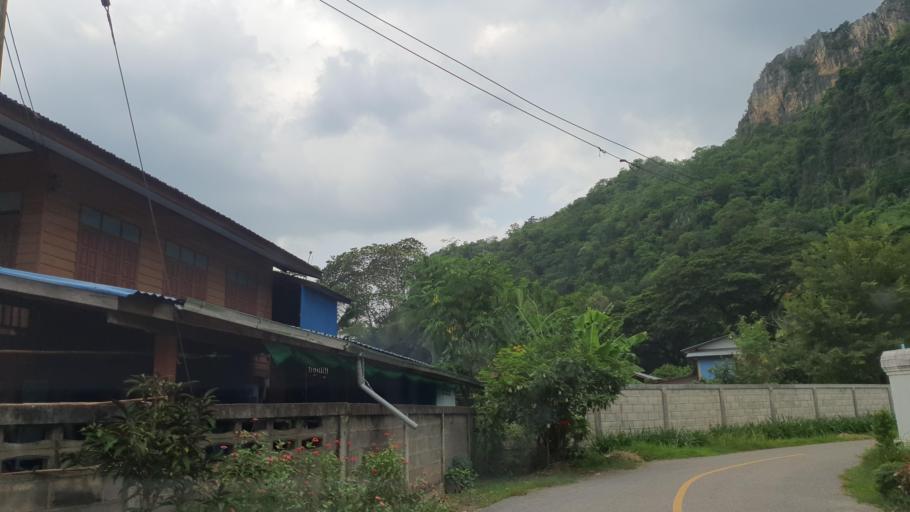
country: TH
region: Sukhothai
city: Thung Saliam
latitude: 17.3200
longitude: 99.5116
